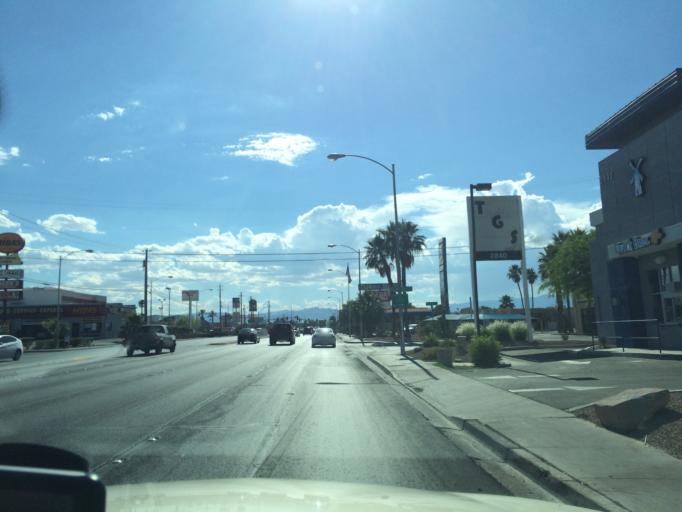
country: US
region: Nevada
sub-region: Clark County
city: Winchester
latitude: 36.1001
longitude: -115.1118
